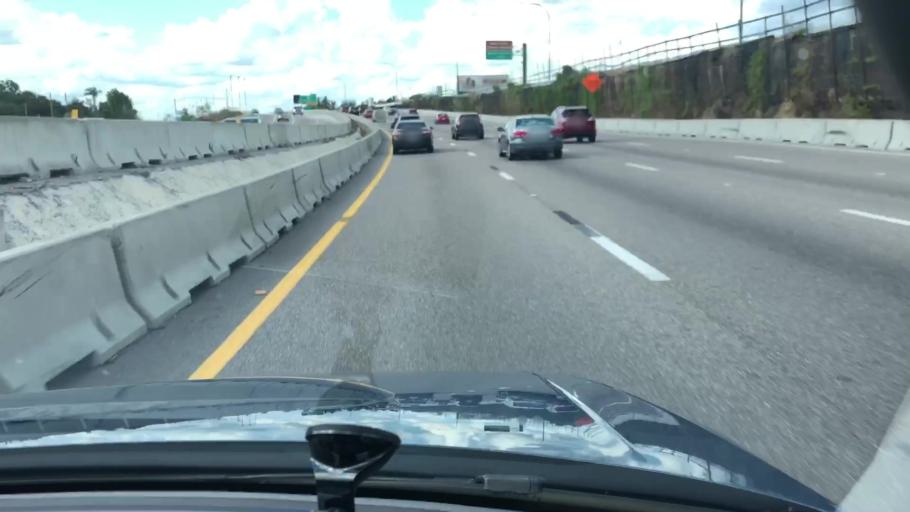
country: US
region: Florida
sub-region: Orange County
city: Fairview Shores
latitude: 28.5873
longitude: -81.3761
